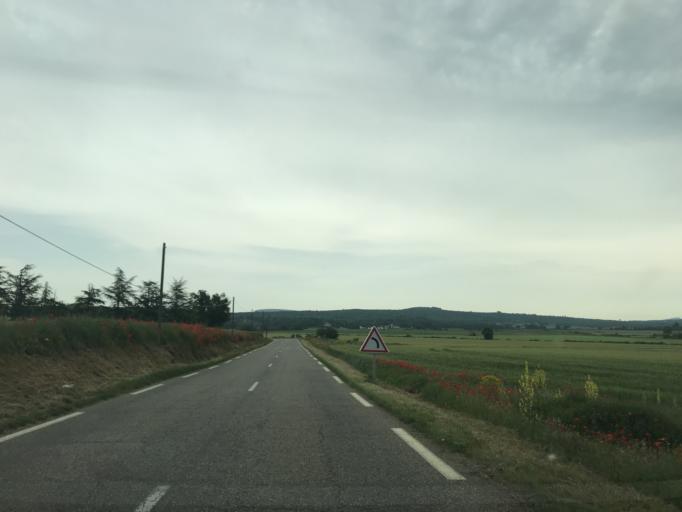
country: FR
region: Provence-Alpes-Cote d'Azur
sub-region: Departement du Var
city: Ginasservis
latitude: 43.6437
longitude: 5.8265
